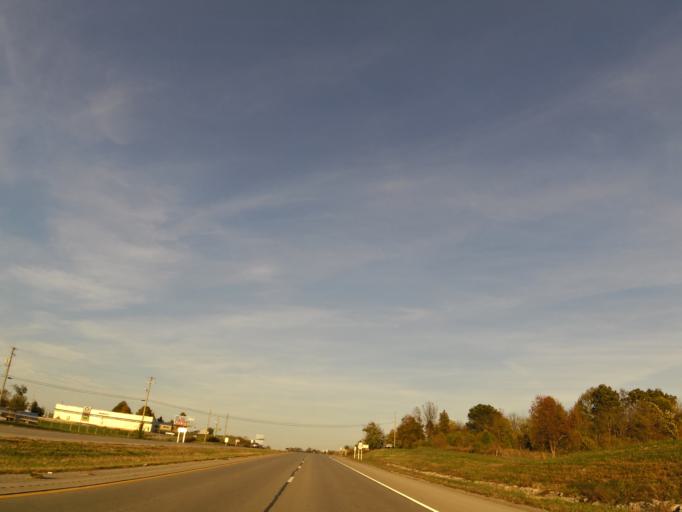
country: US
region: Kentucky
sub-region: Garrard County
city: Lancaster
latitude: 37.7067
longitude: -84.6554
